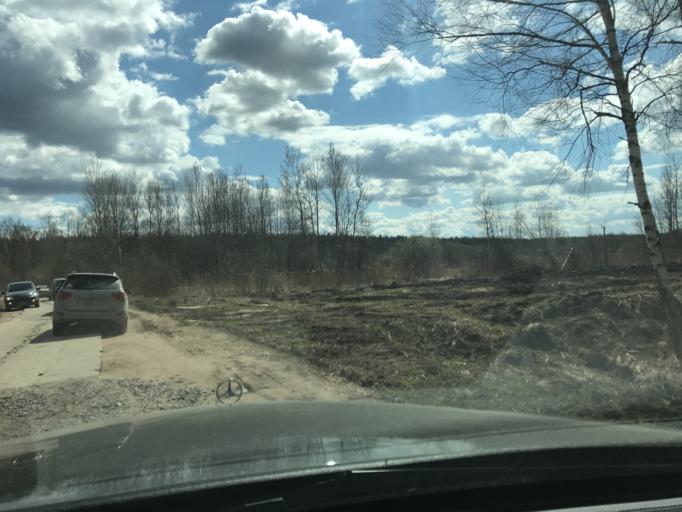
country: RU
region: Moskovskaya
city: Vereya
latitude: 55.8396
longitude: 39.0802
